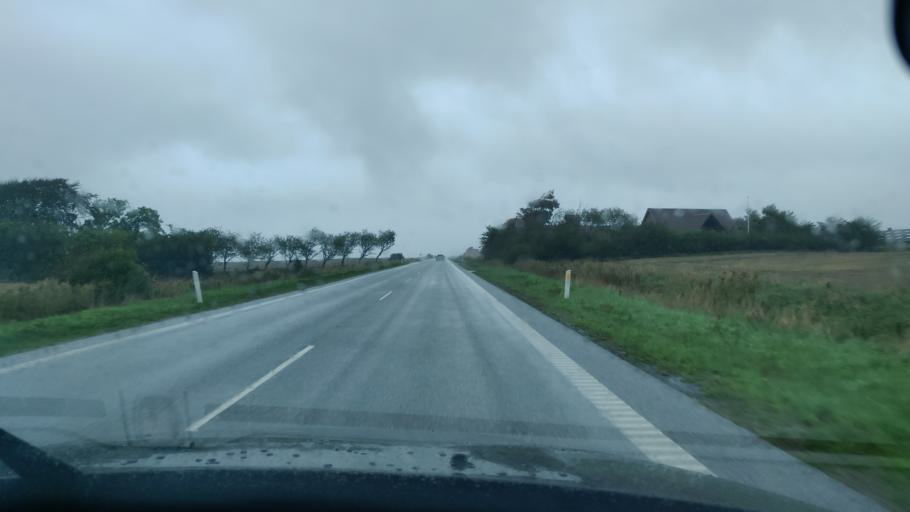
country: DK
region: North Denmark
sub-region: Thisted Kommune
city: Hurup
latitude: 56.8573
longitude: 8.5482
